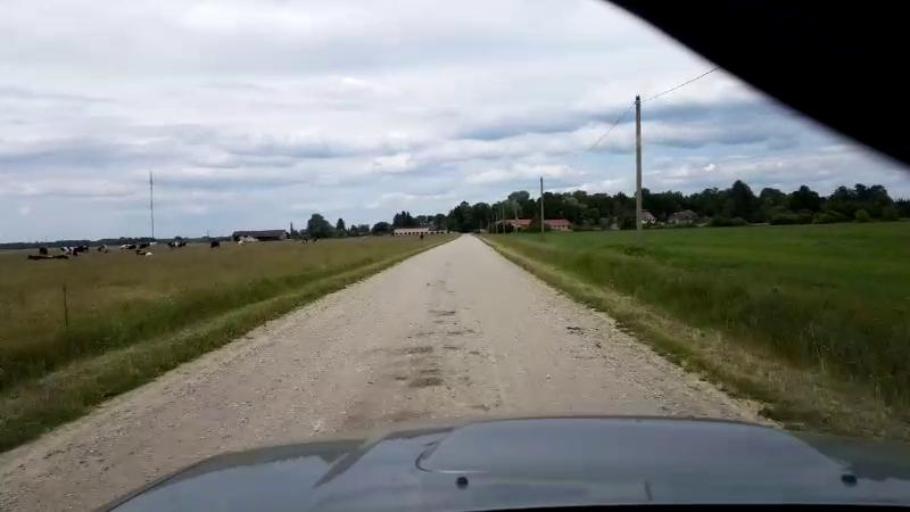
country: EE
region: Paernumaa
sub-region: Halinga vald
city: Parnu-Jaagupi
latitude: 58.5269
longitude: 24.5845
